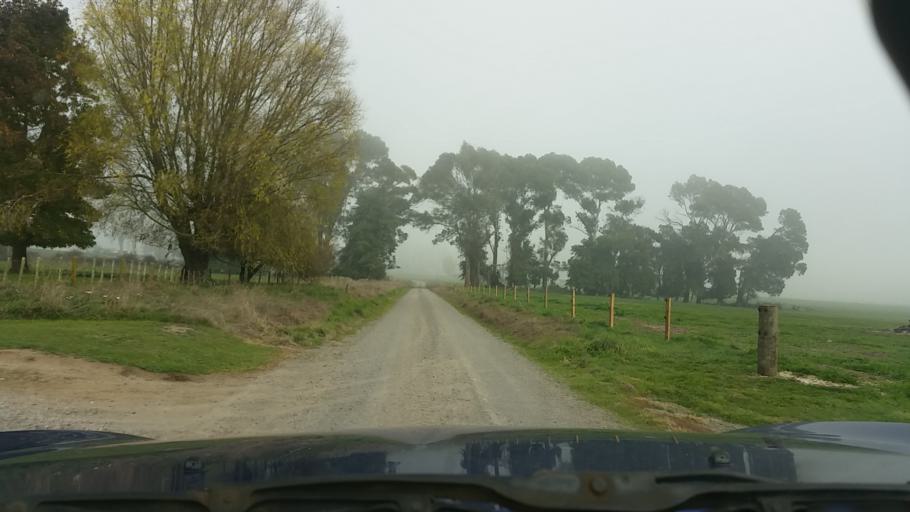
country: NZ
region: Waikato
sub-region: Taupo District
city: Taupo
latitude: -38.5200
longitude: 176.3681
